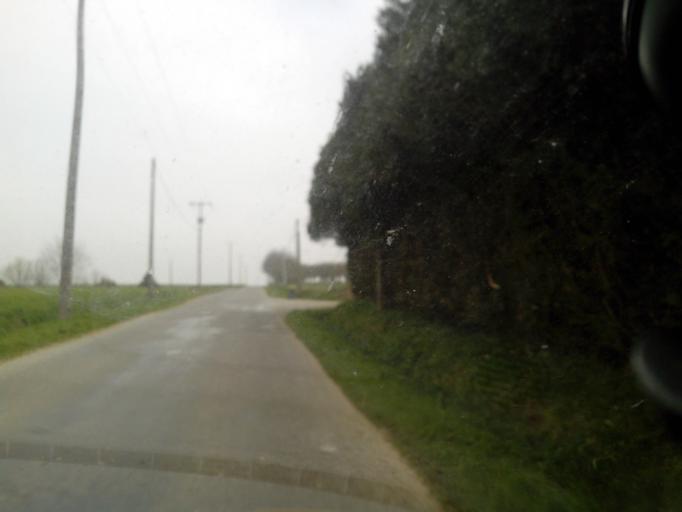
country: FR
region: Brittany
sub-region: Departement d'Ille-et-Vilaine
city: Gael
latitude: 48.1671
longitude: -2.2611
